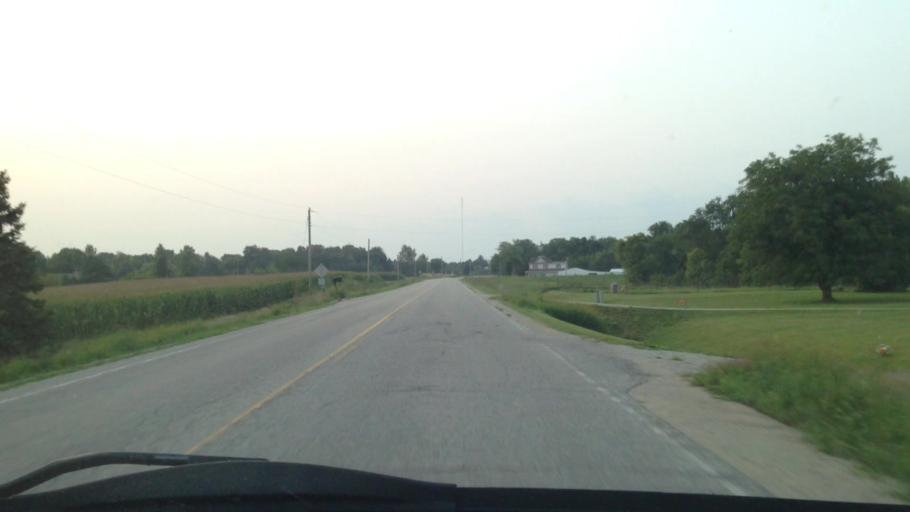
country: US
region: Iowa
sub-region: Benton County
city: Urbana
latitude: 42.1397
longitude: -91.8772
